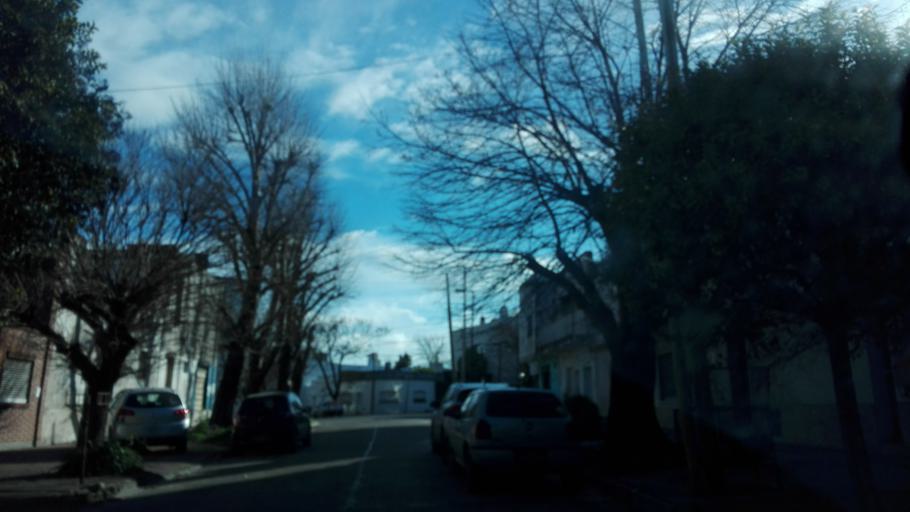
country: AR
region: Buenos Aires
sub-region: Partido de La Plata
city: La Plata
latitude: -34.9362
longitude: -57.9472
